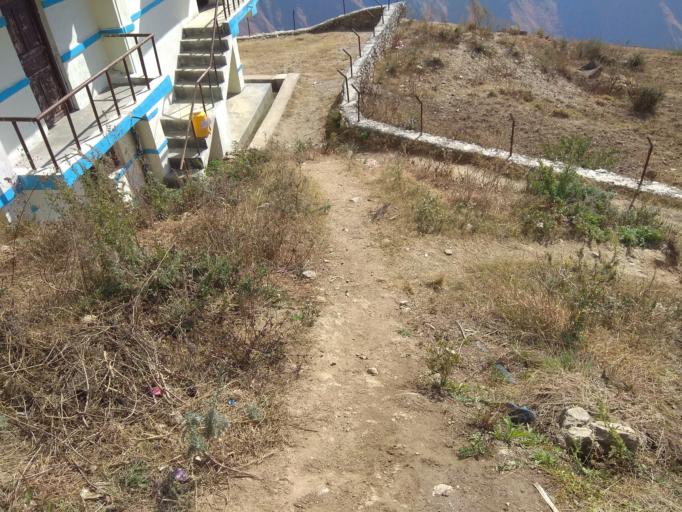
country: NP
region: Mid Western
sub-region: Bheri Zone
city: Dailekh
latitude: 29.2946
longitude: 81.7212
